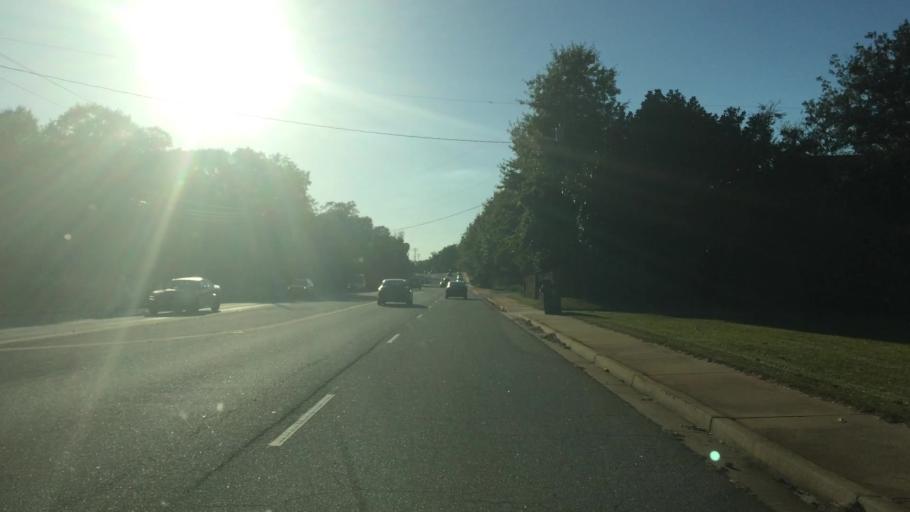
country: US
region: South Carolina
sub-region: Greenville County
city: Wade Hampton
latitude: 34.8567
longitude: -82.3026
